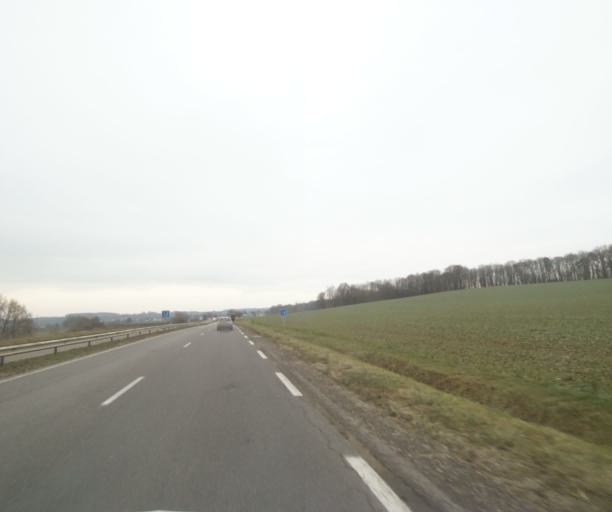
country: FR
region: Lorraine
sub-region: Departement de la Meuse
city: Ancerville
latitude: 48.6088
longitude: 5.0138
